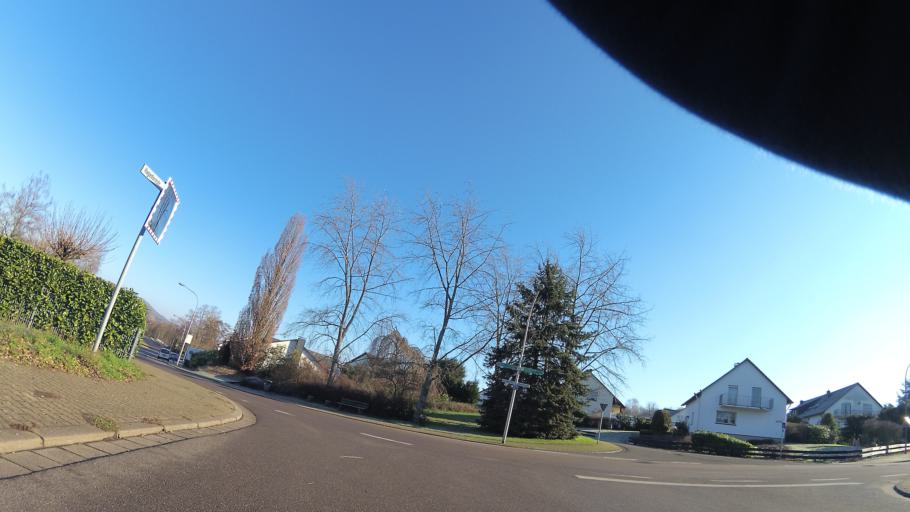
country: DE
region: Saarland
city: Saarlouis
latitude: 49.2996
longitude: 6.7450
